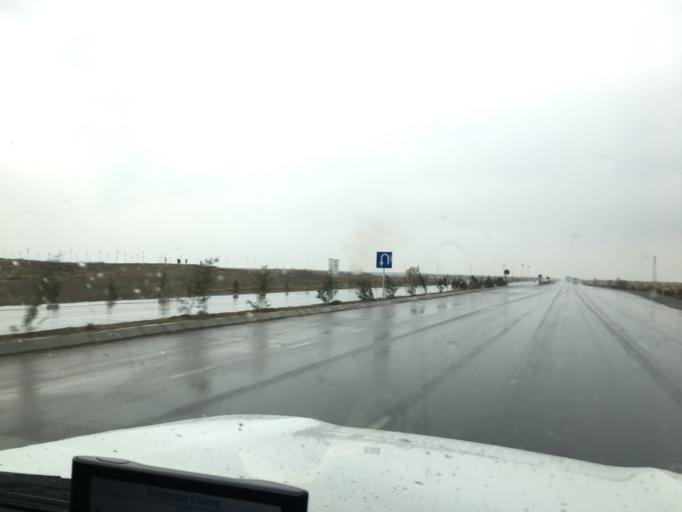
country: TM
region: Ahal
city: Annau
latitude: 37.8613
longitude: 58.6775
